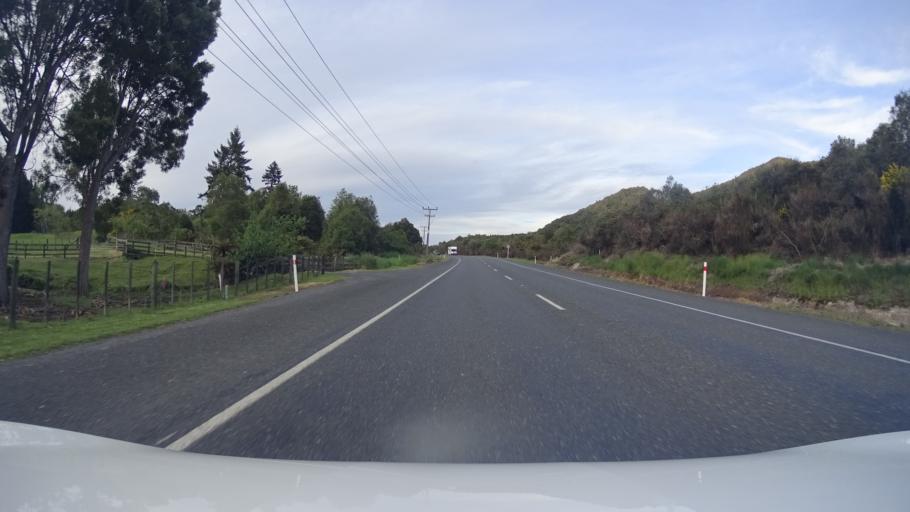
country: NZ
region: Bay of Plenty
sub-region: Rotorua District
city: Rotorua
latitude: -38.3209
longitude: 176.3731
